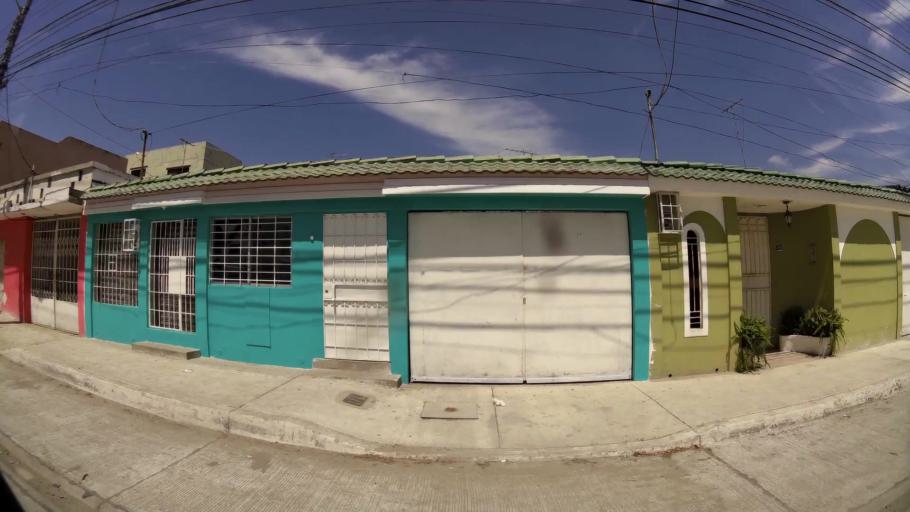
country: EC
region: Guayas
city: Eloy Alfaro
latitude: -2.1137
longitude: -79.9048
